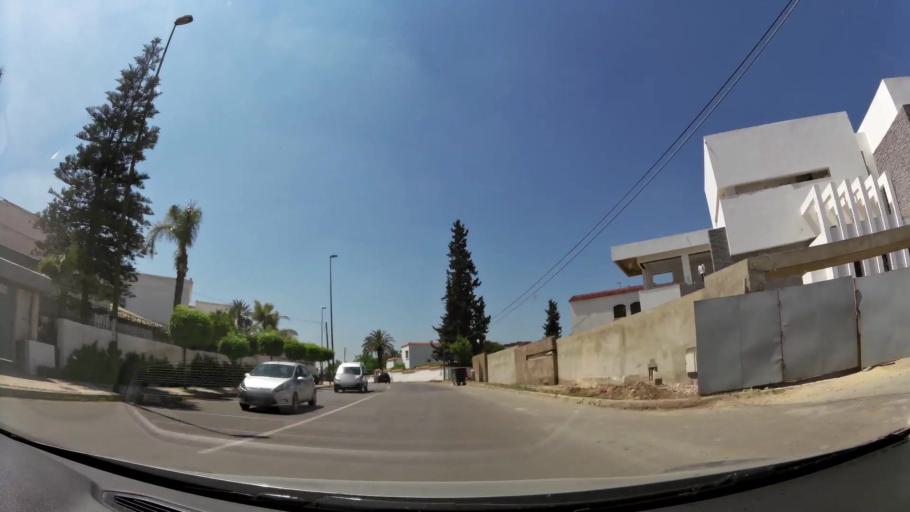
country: MA
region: Fes-Boulemane
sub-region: Fes
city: Fes
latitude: 34.0298
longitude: -5.0144
